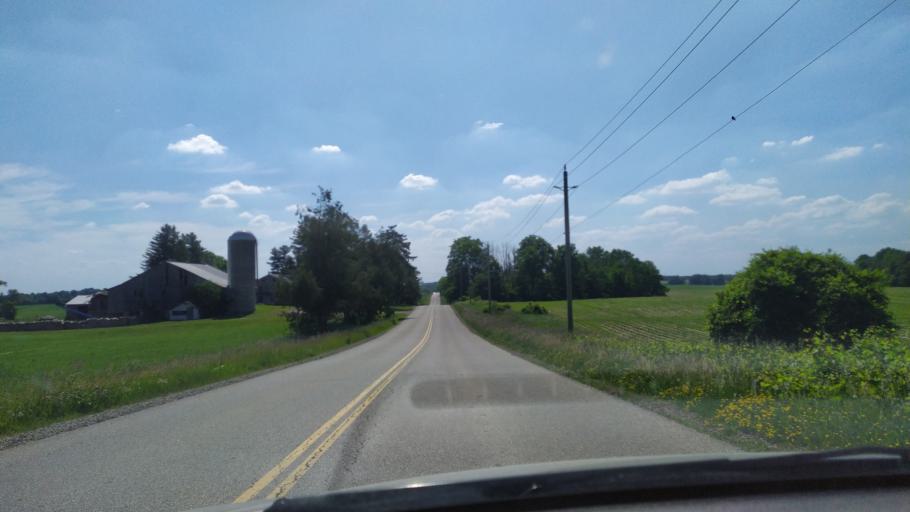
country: CA
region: Ontario
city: Kitchener
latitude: 43.3617
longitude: -80.6208
